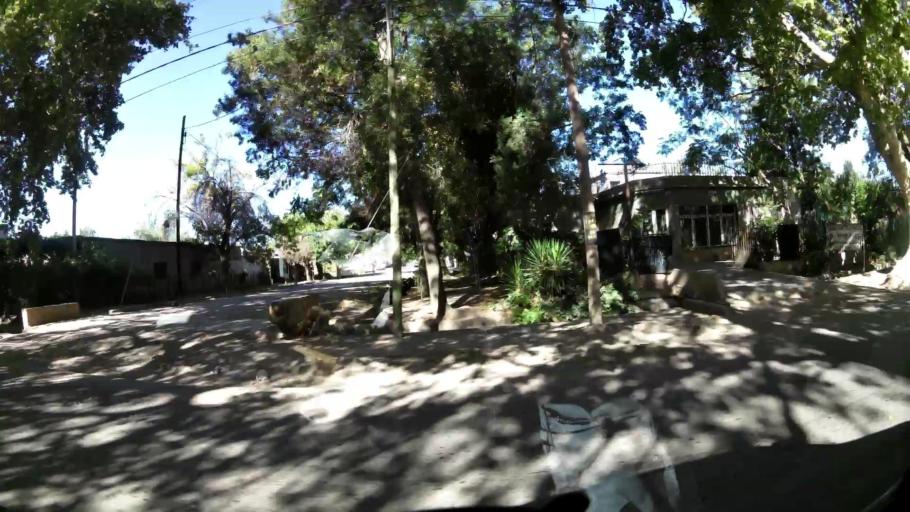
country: AR
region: Mendoza
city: Las Heras
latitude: -32.8339
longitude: -68.8246
